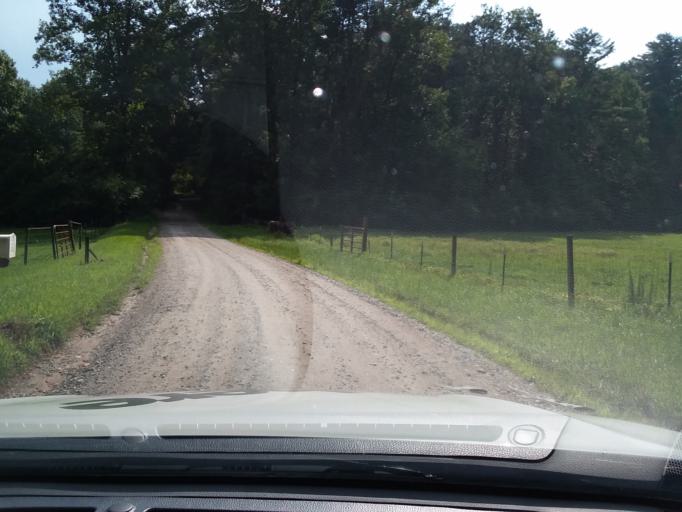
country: US
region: Georgia
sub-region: Habersham County
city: Clarkesville
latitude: 34.7196
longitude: -83.4431
